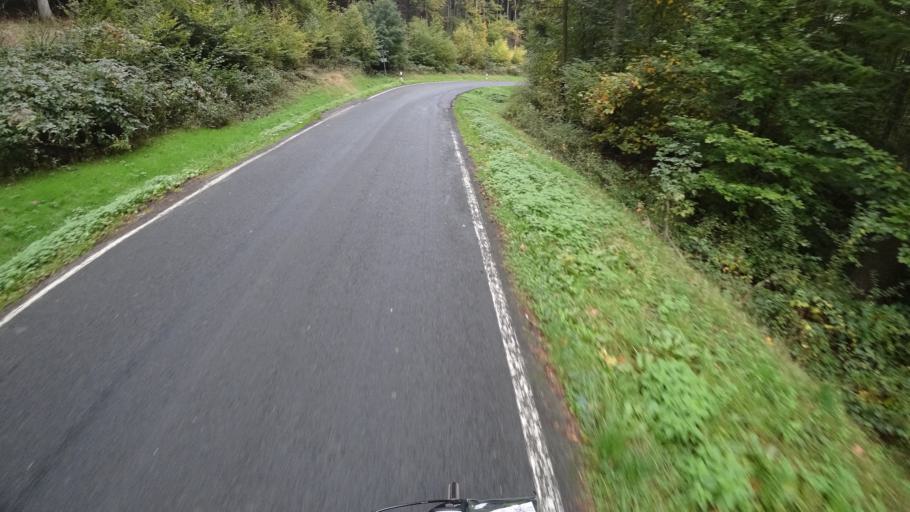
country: DE
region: Rheinland-Pfalz
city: Oberhaid
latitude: 50.5133
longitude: 7.7279
